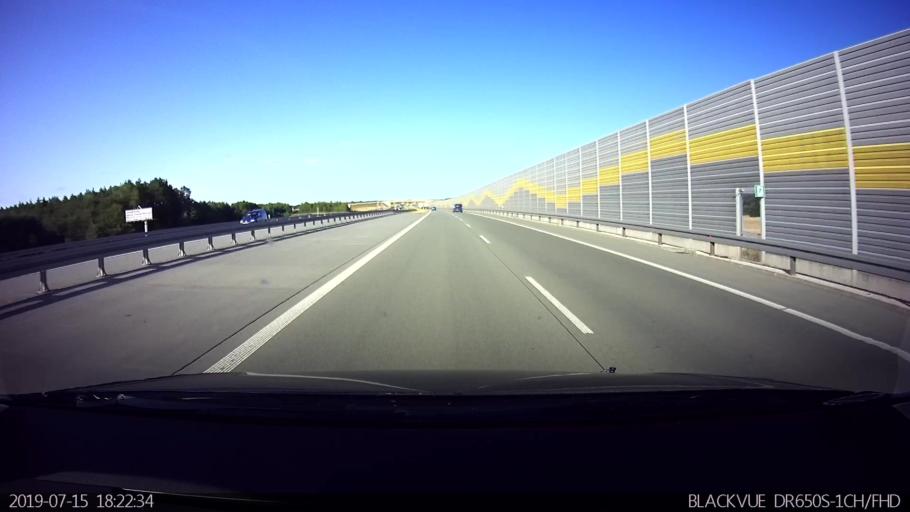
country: PL
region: Lodz Voivodeship
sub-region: Powiat laski
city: Lask
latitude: 51.5554
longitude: 19.1095
